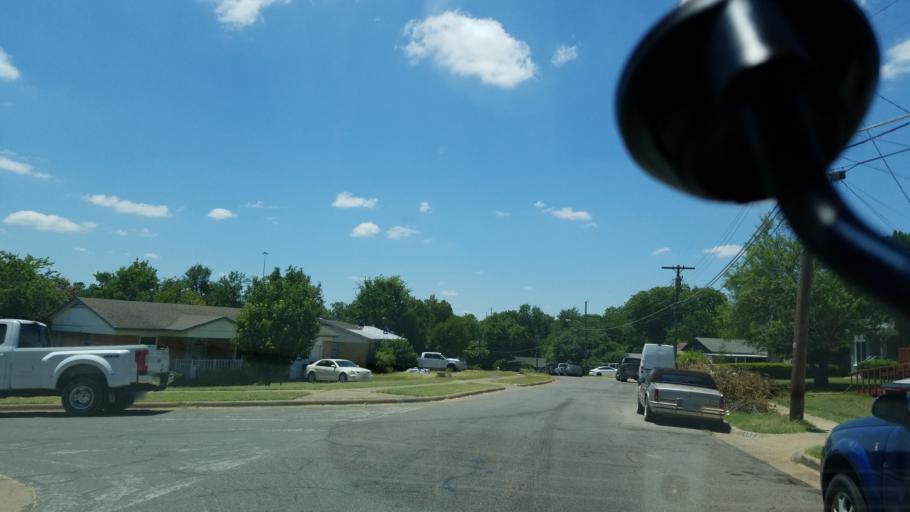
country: US
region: Texas
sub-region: Dallas County
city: Cockrell Hill
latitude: 32.6961
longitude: -96.8187
